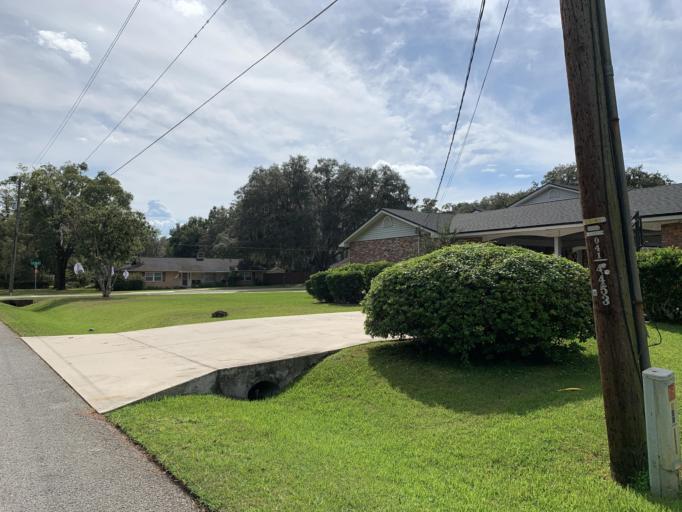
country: US
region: Florida
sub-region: Marion County
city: Ocala
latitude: 29.1785
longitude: -82.1052
